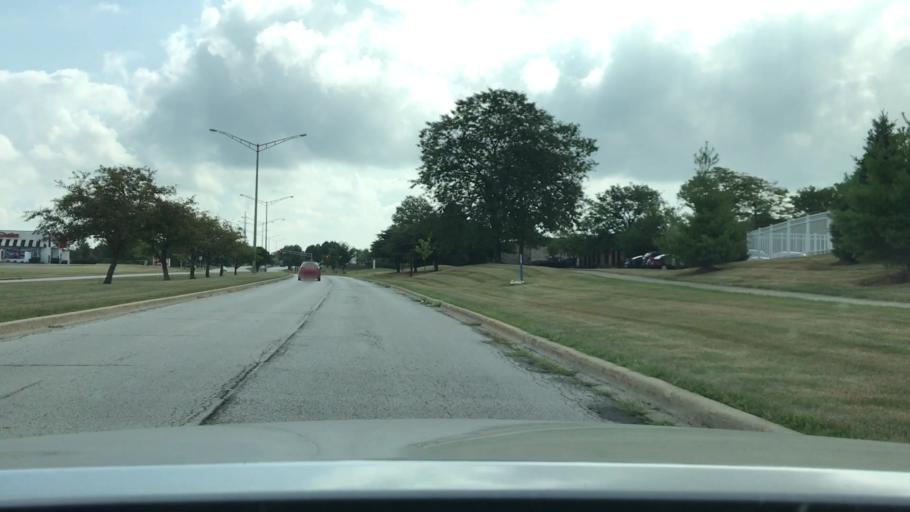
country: US
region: Illinois
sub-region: DuPage County
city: Naperville
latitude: 41.7549
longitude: -88.2125
